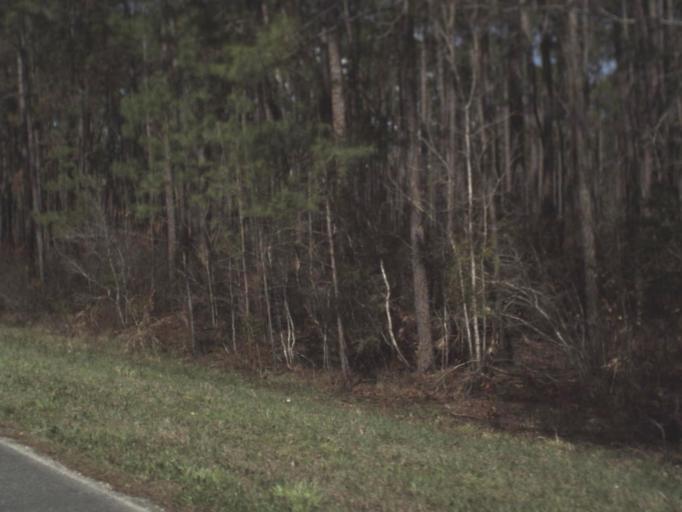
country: US
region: Florida
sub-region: Gadsden County
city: Midway
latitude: 30.3864
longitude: -84.5726
